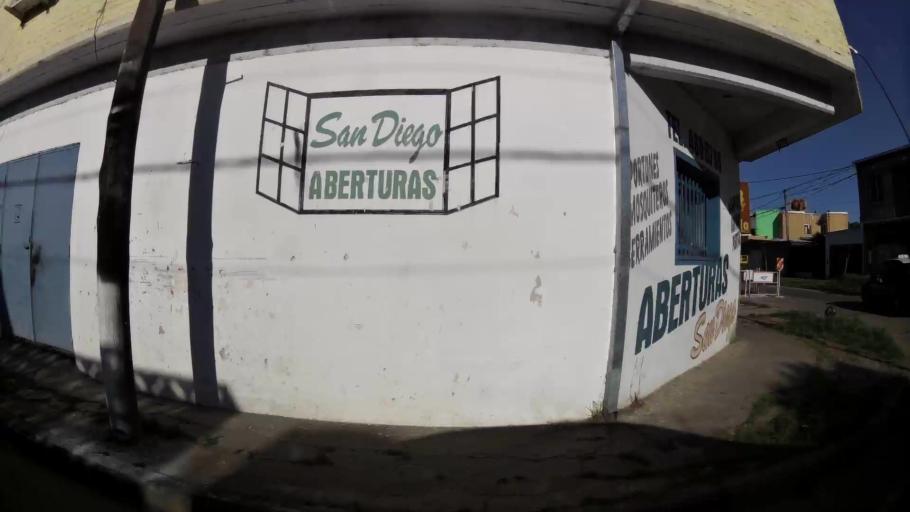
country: AR
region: Santa Fe
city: Santa Fe de la Vera Cruz
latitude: -31.6108
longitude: -60.6995
